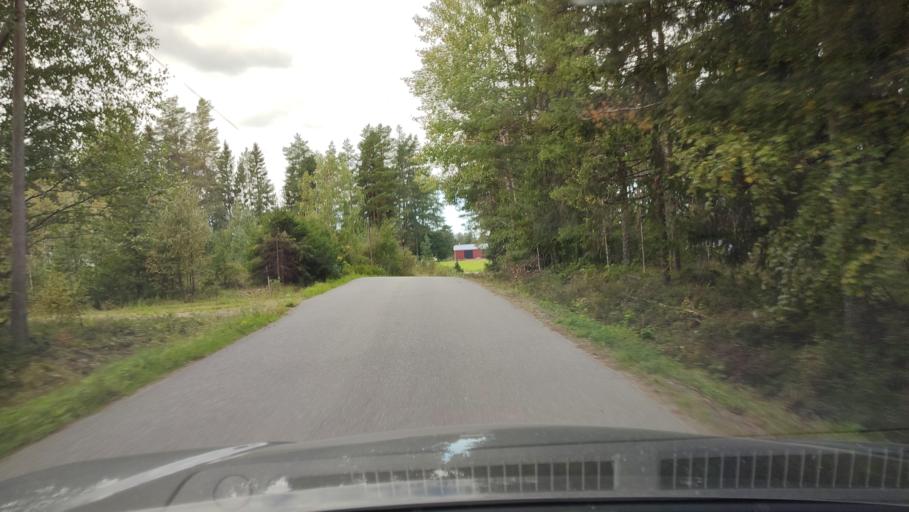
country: FI
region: Southern Ostrobothnia
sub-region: Suupohja
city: Karijoki
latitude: 62.2369
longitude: 21.5959
